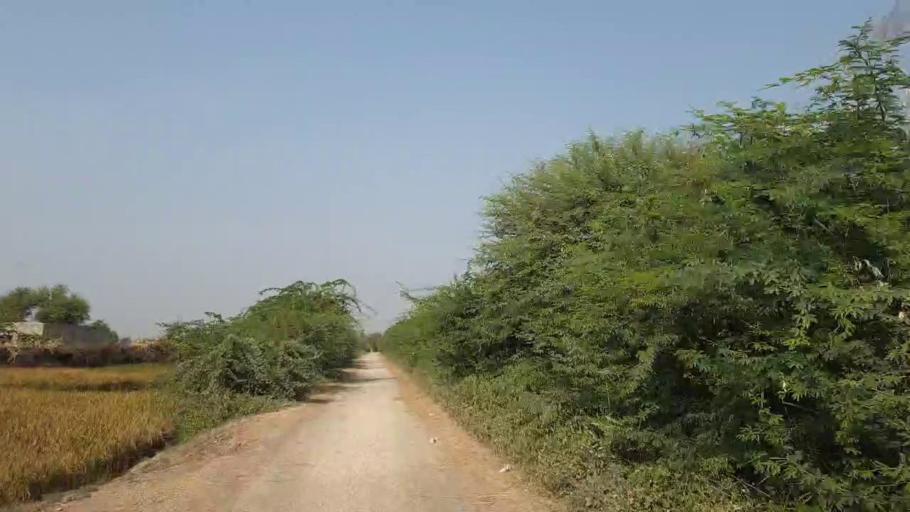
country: PK
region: Sindh
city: Matli
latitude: 24.9482
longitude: 68.5566
